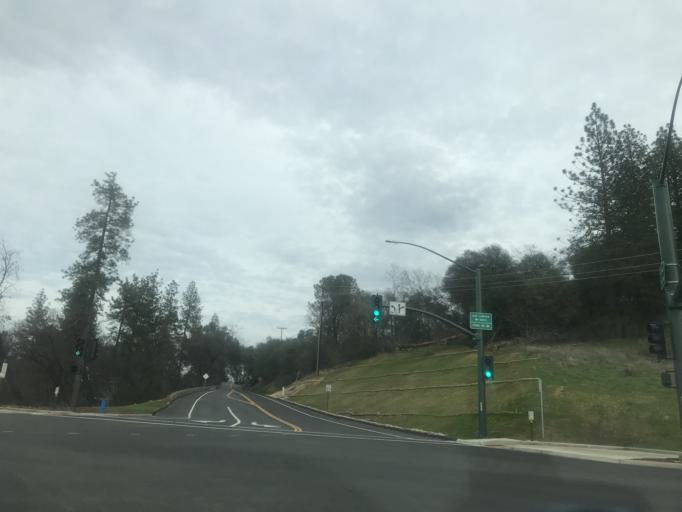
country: US
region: California
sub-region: El Dorado County
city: Placerville
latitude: 38.7267
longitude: -120.8237
